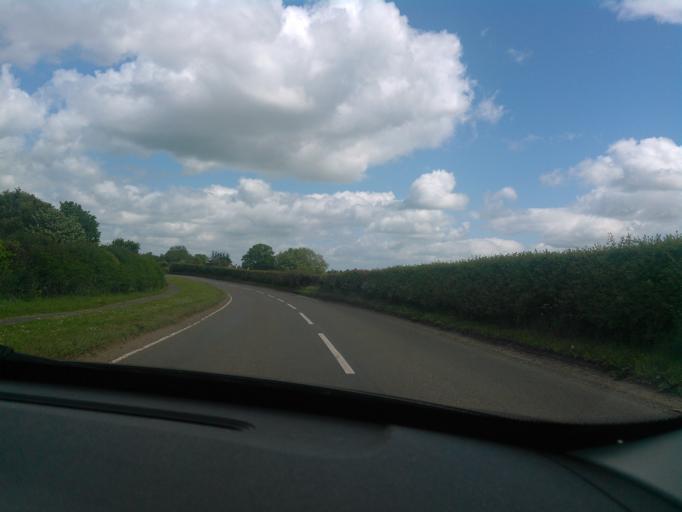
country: GB
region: England
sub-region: Shropshire
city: Wem
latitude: 52.8613
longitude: -2.7033
